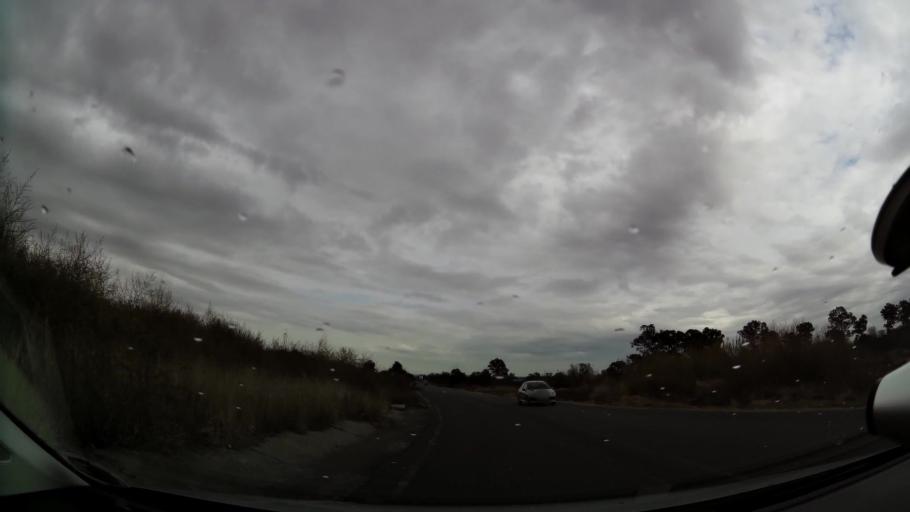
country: ZA
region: Orange Free State
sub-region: Fezile Dabi District Municipality
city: Kroonstad
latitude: -27.6508
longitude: 27.2269
